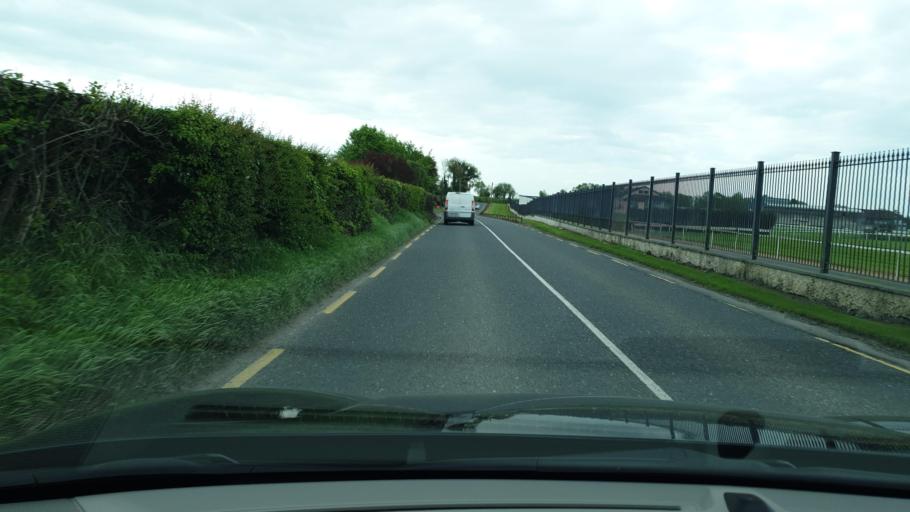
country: IE
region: Leinster
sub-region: An Mhi
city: Navan
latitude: 53.6868
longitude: -6.6729
